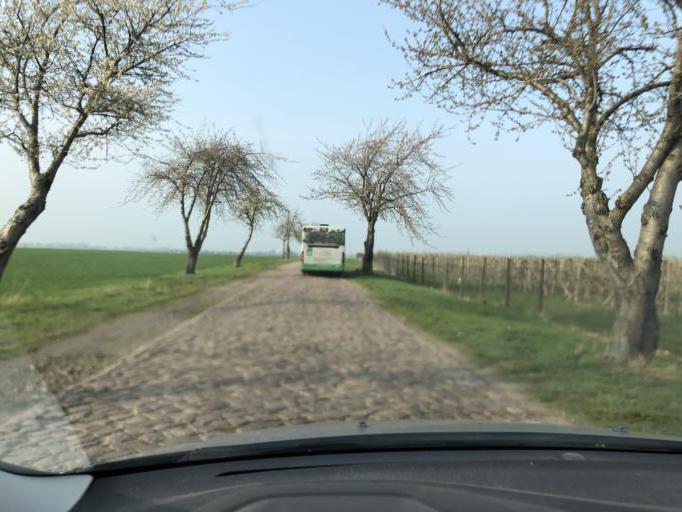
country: DE
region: Saxony-Anhalt
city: Zorbig
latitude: 51.6083
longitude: 12.1105
